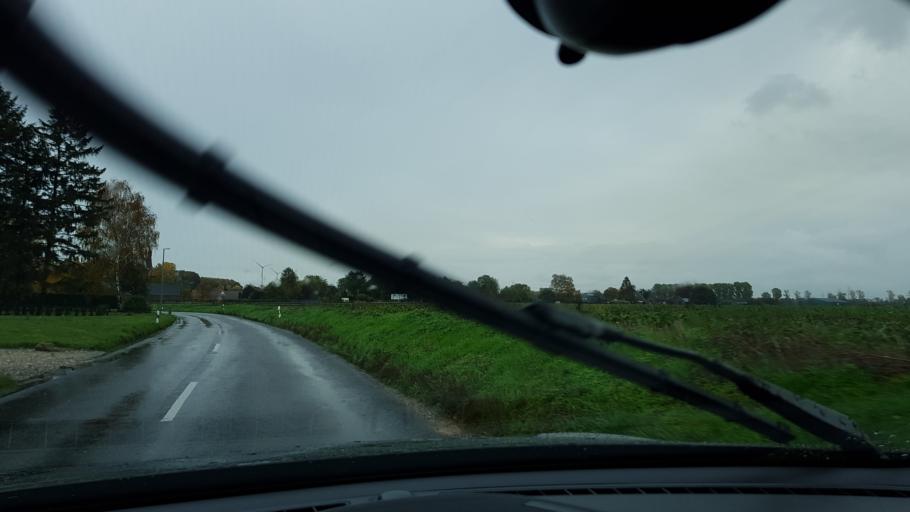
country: DE
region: North Rhine-Westphalia
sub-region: Regierungsbezirk Dusseldorf
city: Rommerskirchen
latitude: 51.0705
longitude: 6.6863
